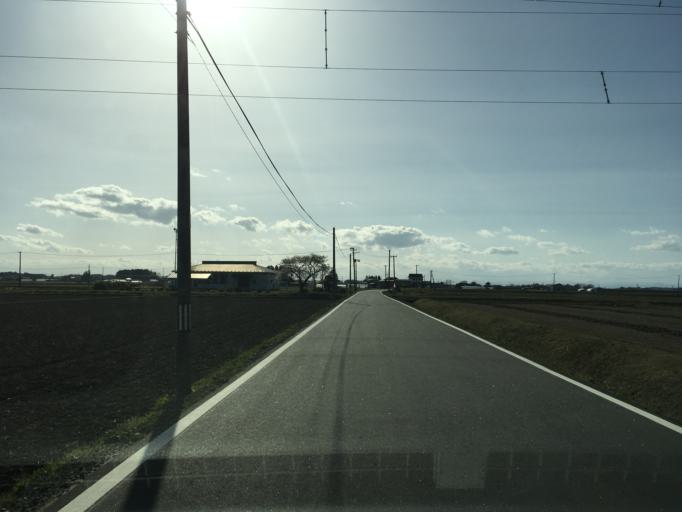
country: JP
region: Miyagi
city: Wakuya
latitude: 38.6596
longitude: 141.2257
